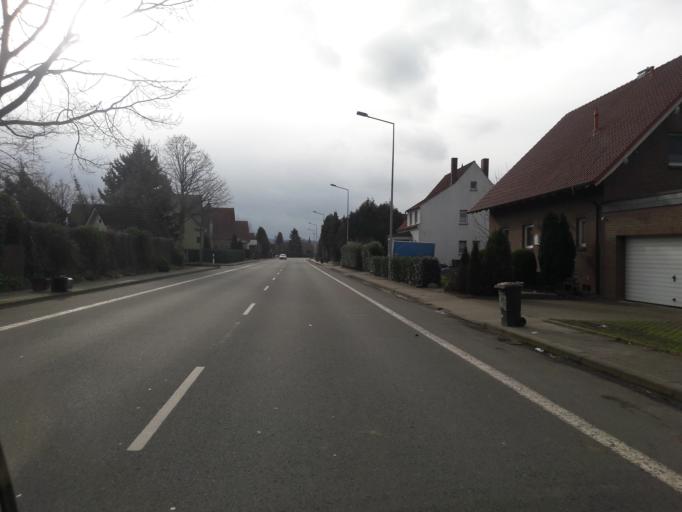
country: DE
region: North Rhine-Westphalia
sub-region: Regierungsbezirk Detmold
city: Hille
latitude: 52.3204
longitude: 8.8296
